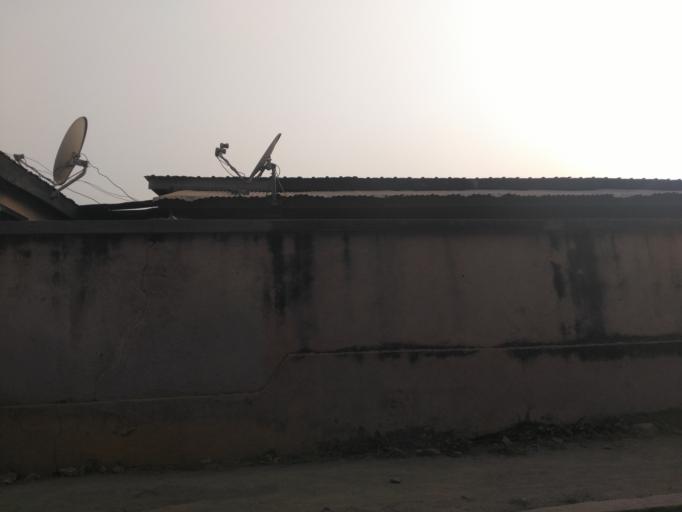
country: GH
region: Ashanti
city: Kumasi
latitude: 6.6809
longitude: -1.5957
